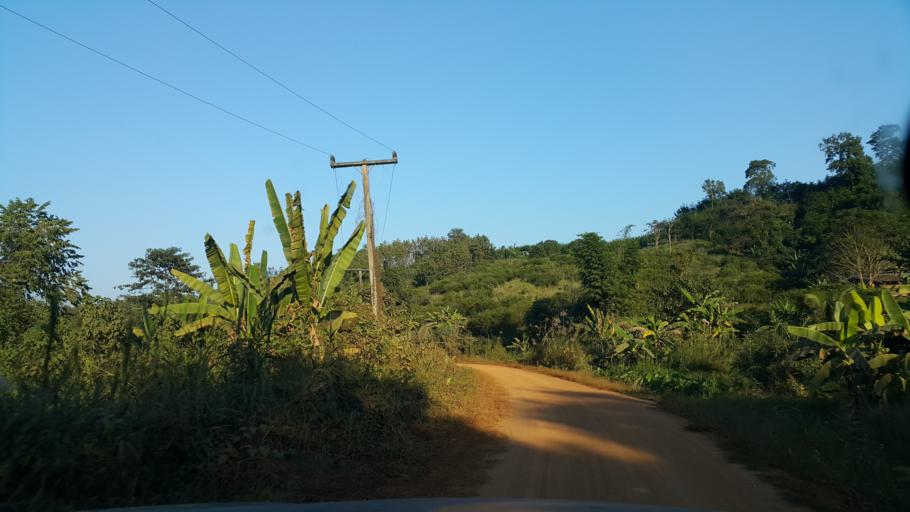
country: TH
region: Sukhothai
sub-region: Amphoe Si Satchanalai
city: Si Satchanalai
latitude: 17.6074
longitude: 99.6177
